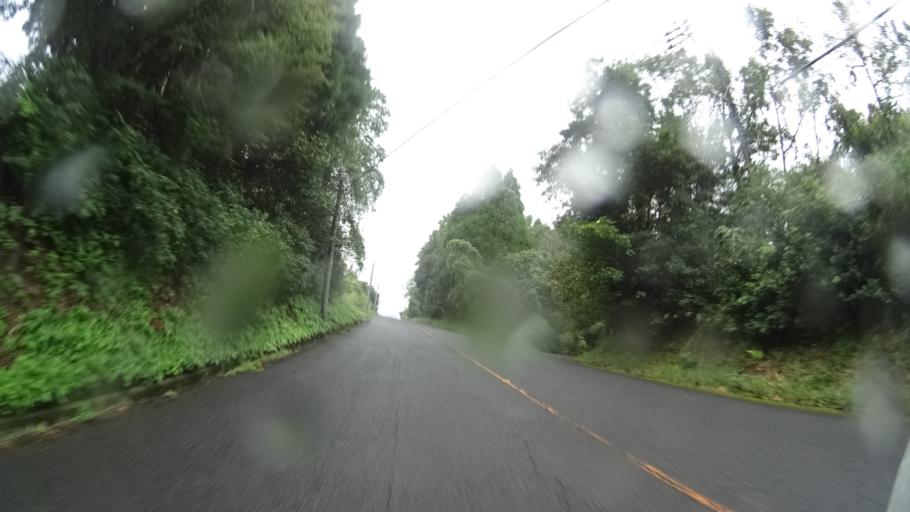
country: JP
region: Kagoshima
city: Kajiki
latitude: 31.7916
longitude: 130.6751
